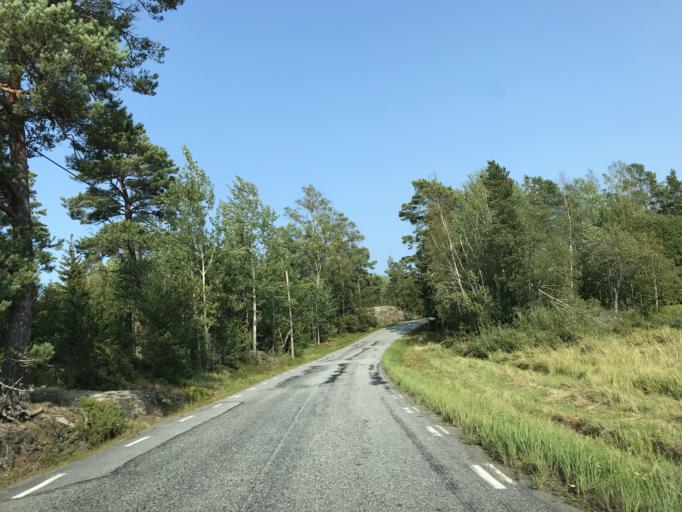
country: SE
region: Stockholm
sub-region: Norrtalje Kommun
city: Bjorko
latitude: 59.8637
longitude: 19.0445
